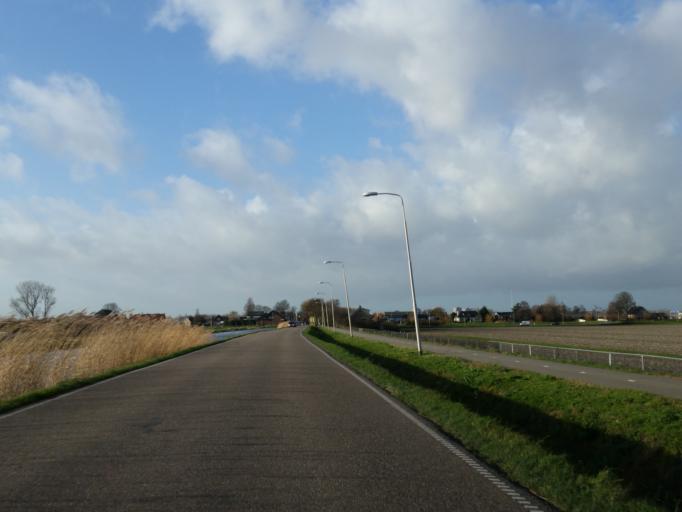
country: NL
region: South Holland
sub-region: Gemeente Rijnwoude
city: Benthuizen
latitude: 52.0430
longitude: 4.5517
